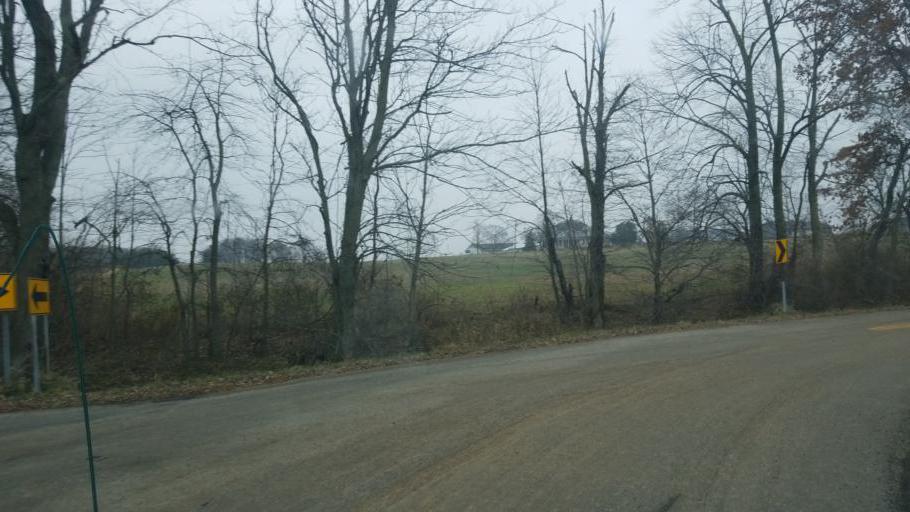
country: US
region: Ohio
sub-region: Huron County
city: New London
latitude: 41.0160
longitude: -82.3549
